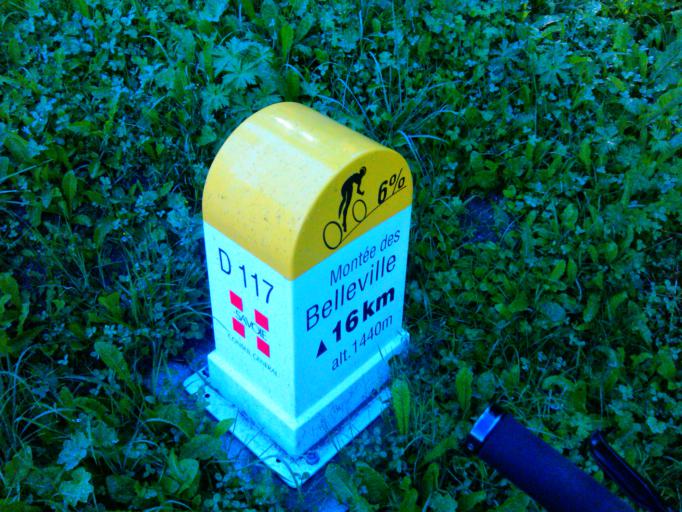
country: FR
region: Rhone-Alpes
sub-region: Departement de la Savoie
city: Saint-Martin-de-Belleville
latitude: 45.3738
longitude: 6.5049
